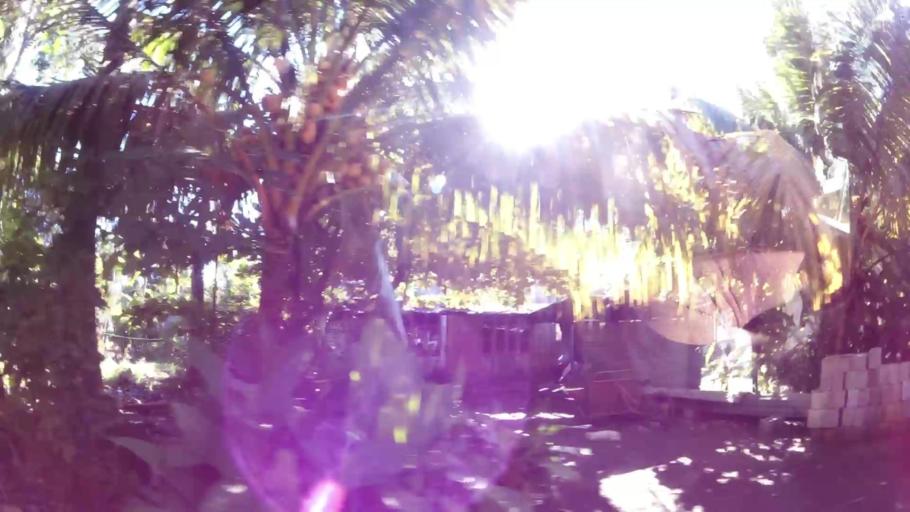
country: GT
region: Santa Rosa
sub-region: Municipio de Taxisco
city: Taxisco
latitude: 13.8967
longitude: -90.4803
